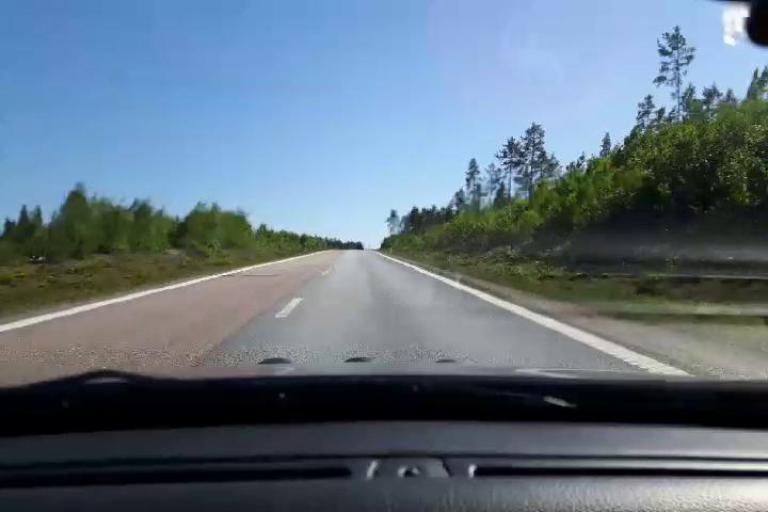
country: SE
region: Gaevleborg
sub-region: Soderhamns Kommun
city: Soderhamn
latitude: 61.3946
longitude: 16.9920
